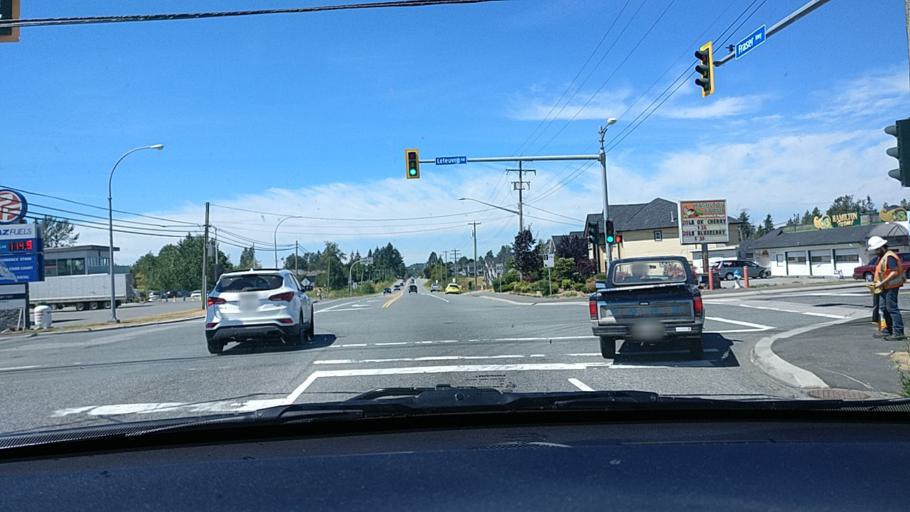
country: CA
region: British Columbia
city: Aldergrove
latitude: 49.0574
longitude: -122.4484
